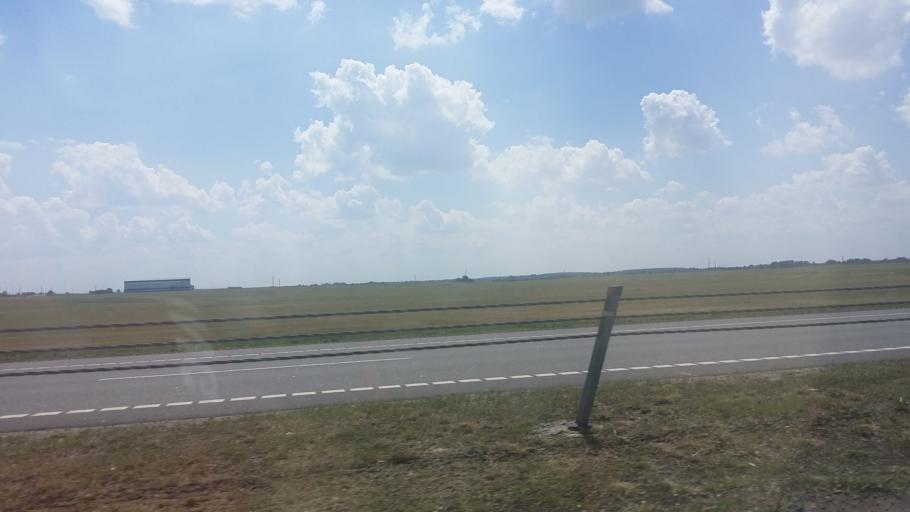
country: BY
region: Minsk
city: Luhavaya Slabada
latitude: 53.7614
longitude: 27.9036
